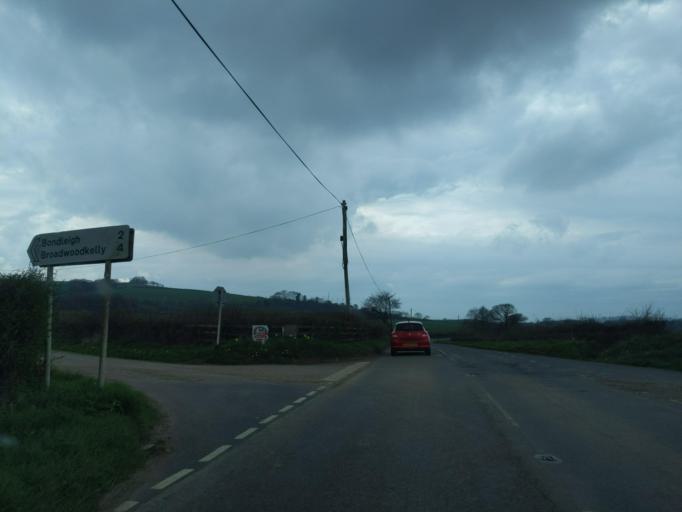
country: GB
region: England
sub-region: Devon
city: Winkleigh
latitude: 50.8448
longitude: -3.8929
